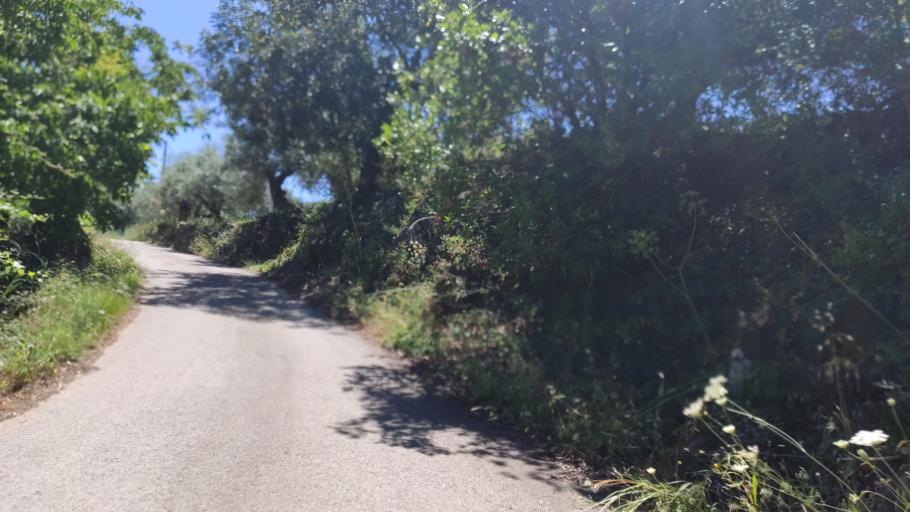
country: PT
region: Faro
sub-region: Sao Bras de Alportel
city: Sao Bras de Alportel
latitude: 37.1737
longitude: -7.9187
